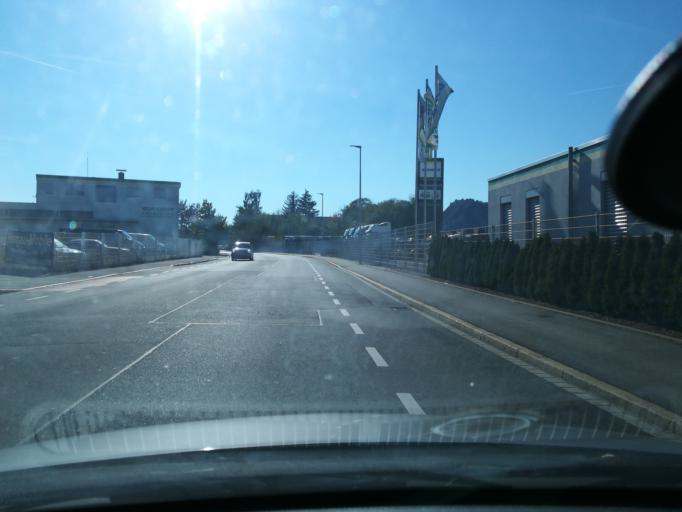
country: DE
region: Baden-Wuerttemberg
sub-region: Freiburg Region
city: Singen
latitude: 47.7570
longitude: 8.8565
